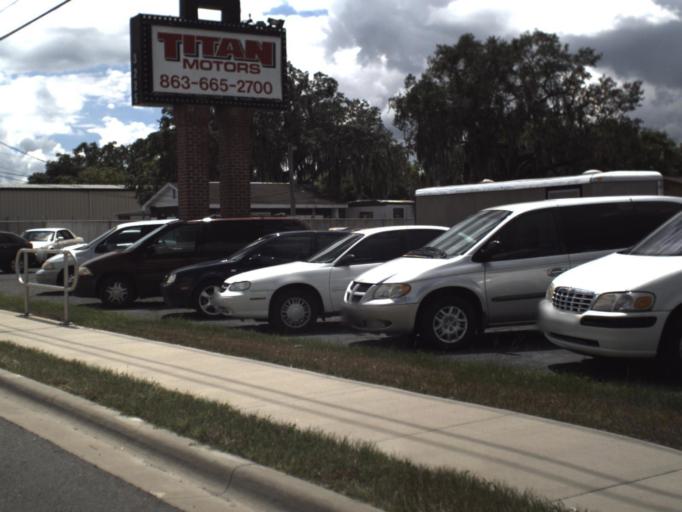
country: US
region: Florida
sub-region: Polk County
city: Crystal Lake
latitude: 28.0094
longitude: -81.9093
